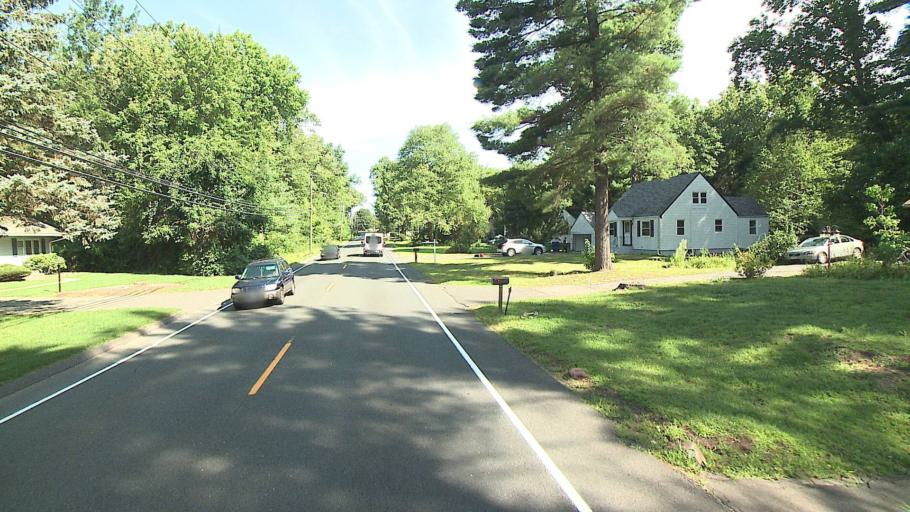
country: US
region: Connecticut
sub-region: Hartford County
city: Blue Hills
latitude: 41.8497
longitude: -72.7015
